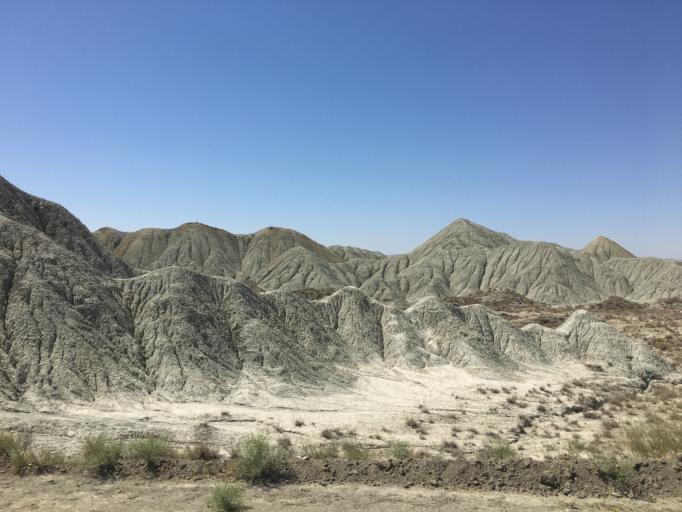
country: TM
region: Balkan
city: Magtymguly
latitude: 38.4550
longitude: 56.2093
